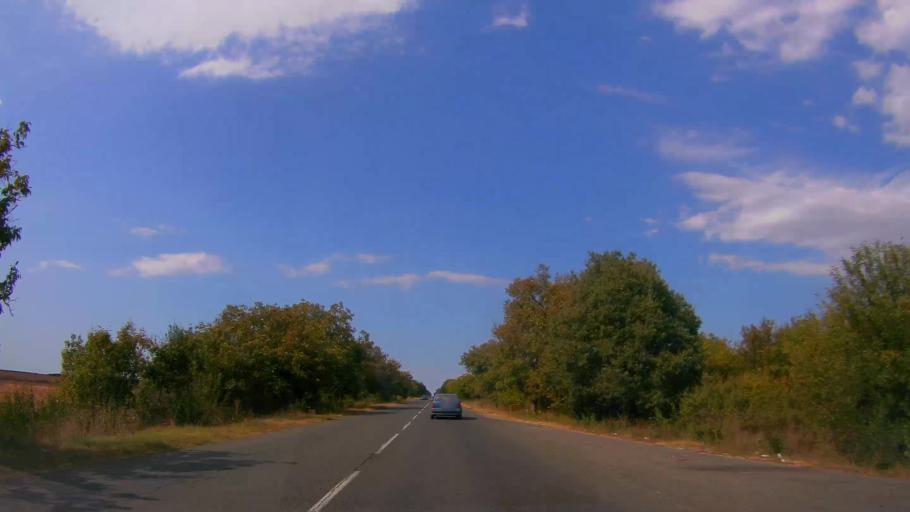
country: BG
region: Burgas
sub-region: Obshtina Aytos
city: Aytos
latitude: 42.6868
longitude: 27.1441
